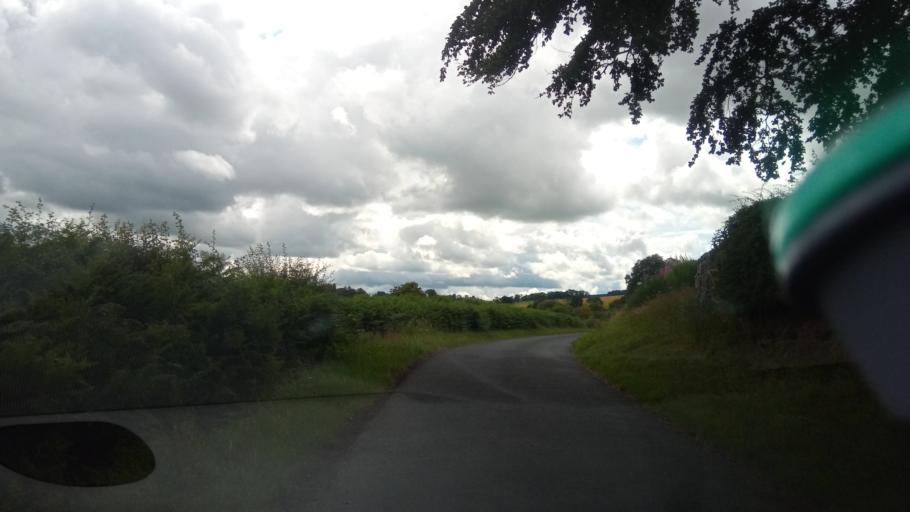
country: GB
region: Scotland
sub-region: The Scottish Borders
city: Kelso
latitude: 55.4897
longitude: -2.4286
